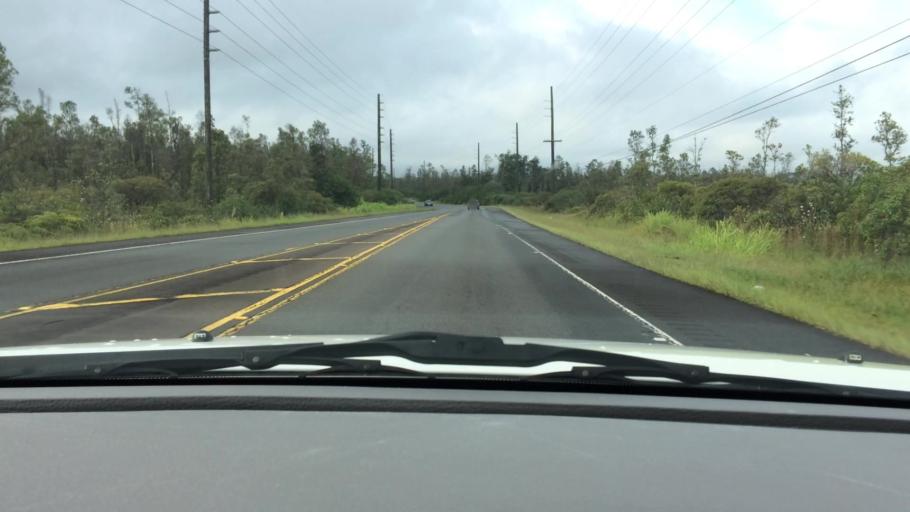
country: US
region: Hawaii
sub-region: Hawaii County
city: Ainaloa
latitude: 19.5290
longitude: -154.9710
